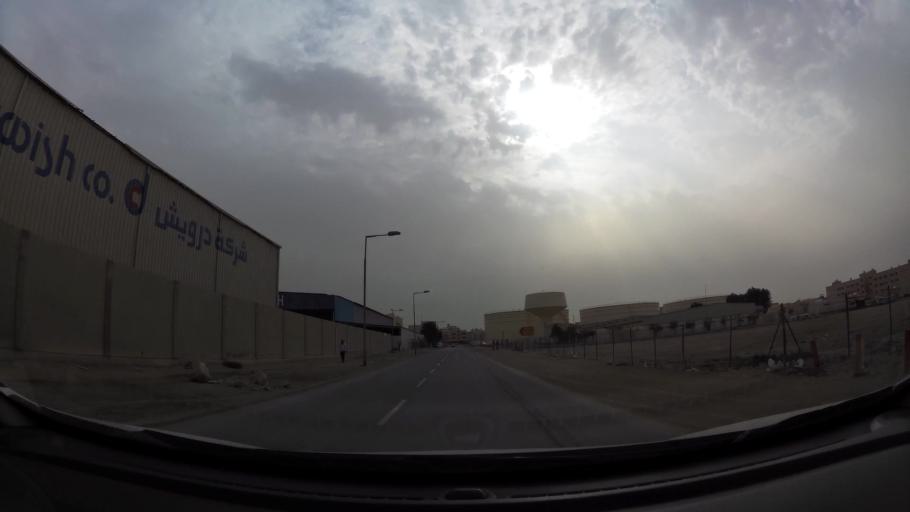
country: BH
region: Northern
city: Ar Rifa'
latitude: 26.1267
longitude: 50.5878
